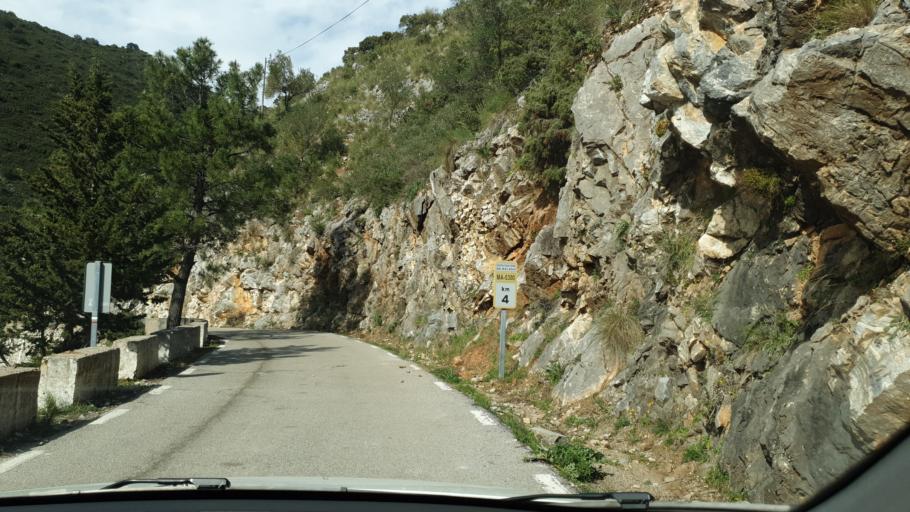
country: ES
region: Andalusia
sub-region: Provincia de Malaga
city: Ojen
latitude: 36.5878
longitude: -4.8799
